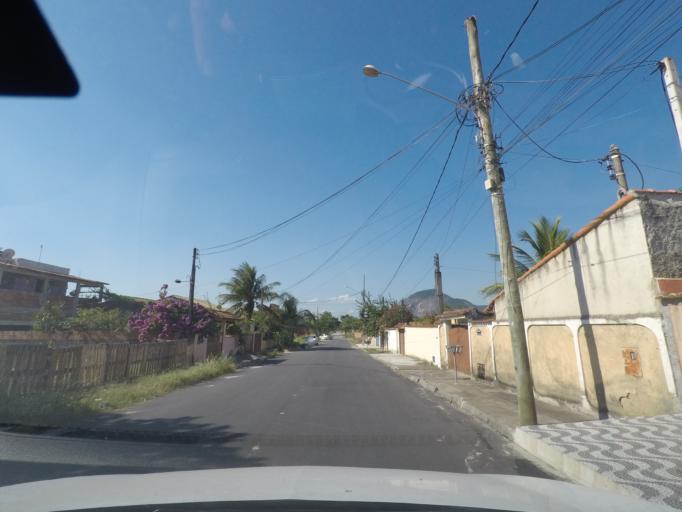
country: BR
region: Rio de Janeiro
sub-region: Marica
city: Marica
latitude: -22.9678
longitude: -42.9235
